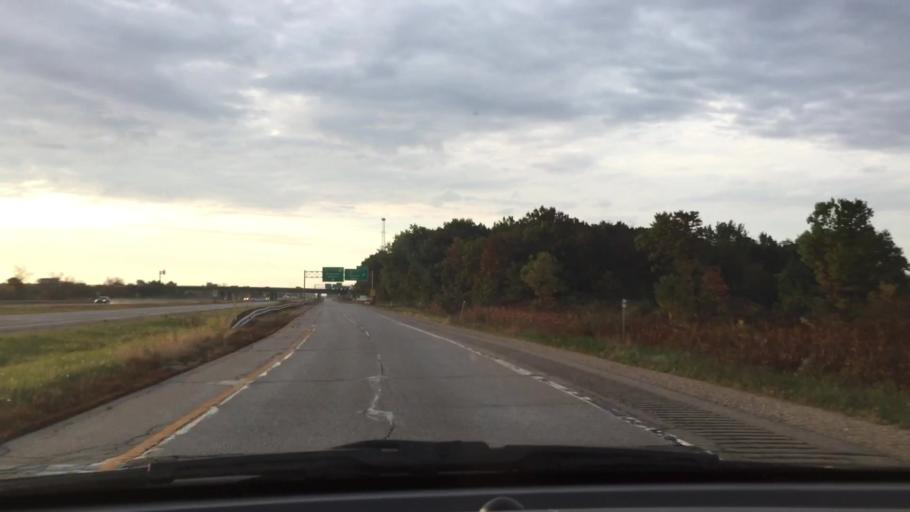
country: US
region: Wisconsin
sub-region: Walworth County
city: Elkhorn
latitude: 42.6786
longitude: -88.5245
